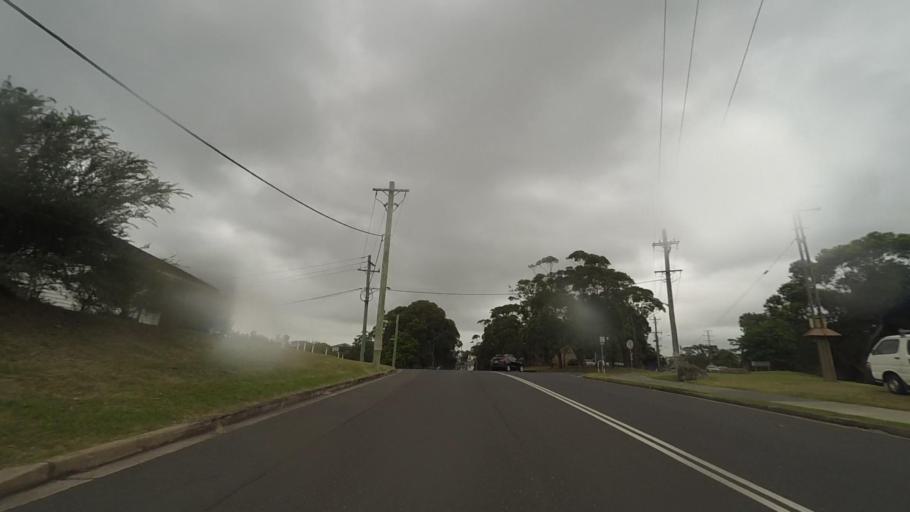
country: AU
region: New South Wales
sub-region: Wollongong
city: Cordeaux Heights
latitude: -34.4464
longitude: 150.8410
